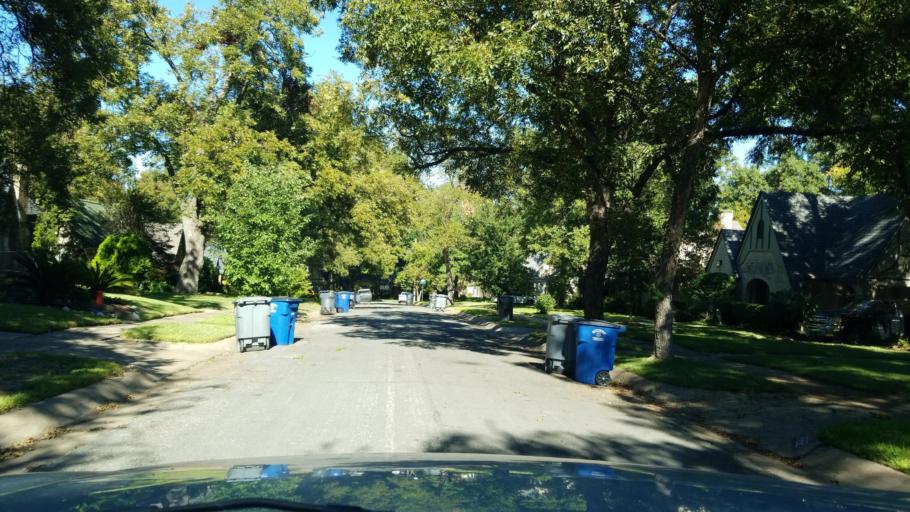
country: US
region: Texas
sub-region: Dallas County
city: Highland Park
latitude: 32.8074
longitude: -96.7420
